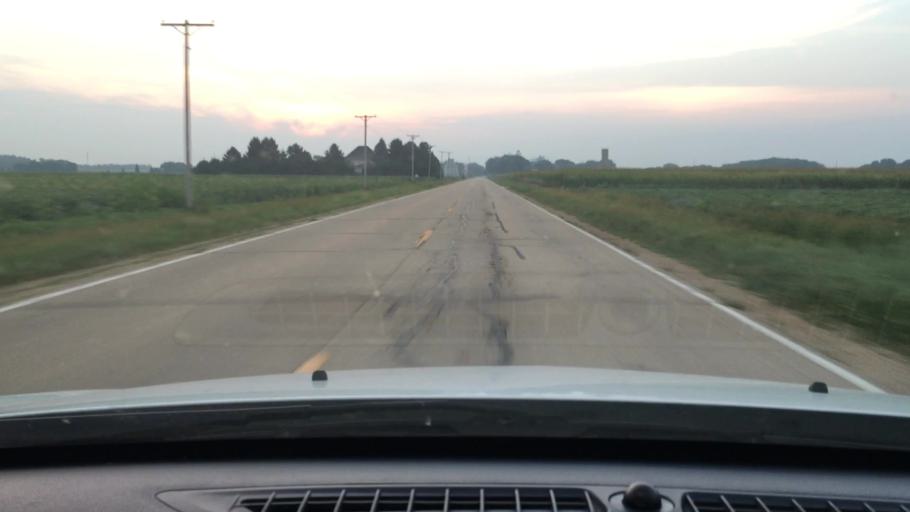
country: US
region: Illinois
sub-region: Ogle County
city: Rochelle
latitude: 41.8473
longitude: -89.0359
